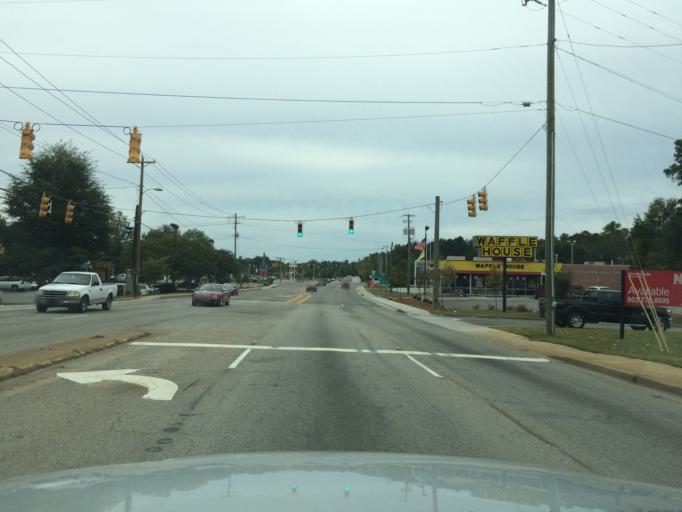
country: US
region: South Carolina
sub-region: Aiken County
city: Aiken
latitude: 33.5782
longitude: -81.7025
